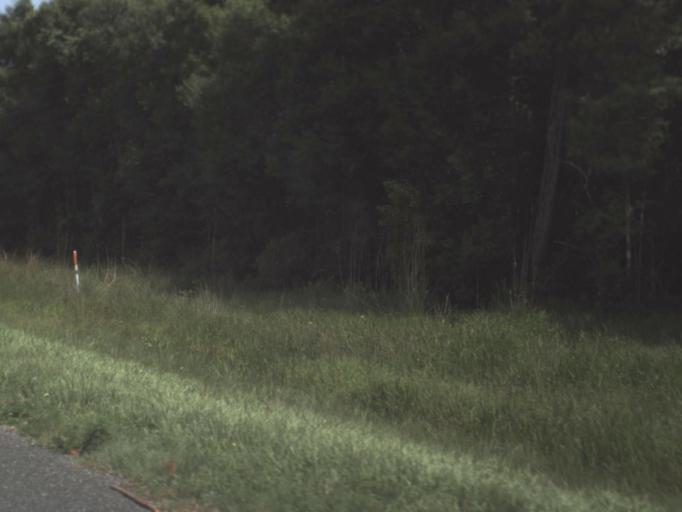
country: US
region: Florida
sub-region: Taylor County
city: Perry
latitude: 29.9777
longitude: -83.4867
